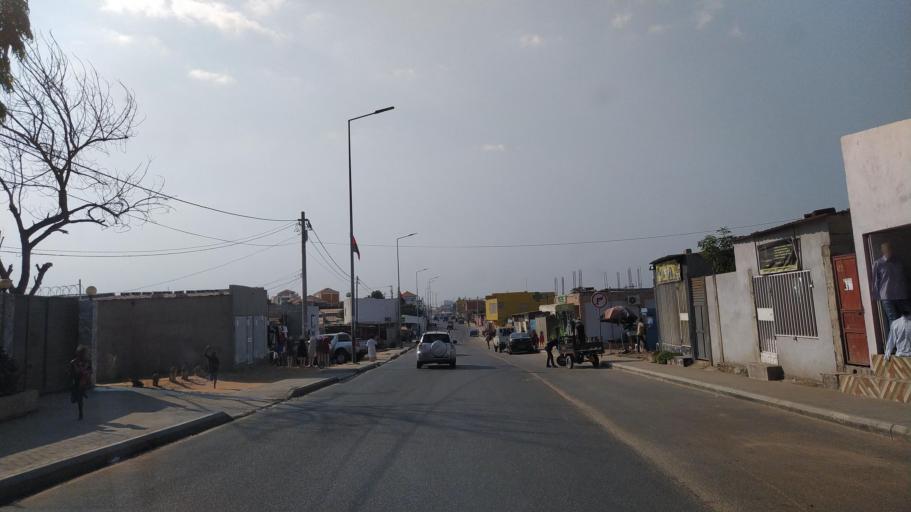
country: AO
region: Luanda
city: Luanda
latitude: -8.8843
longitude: 13.2582
